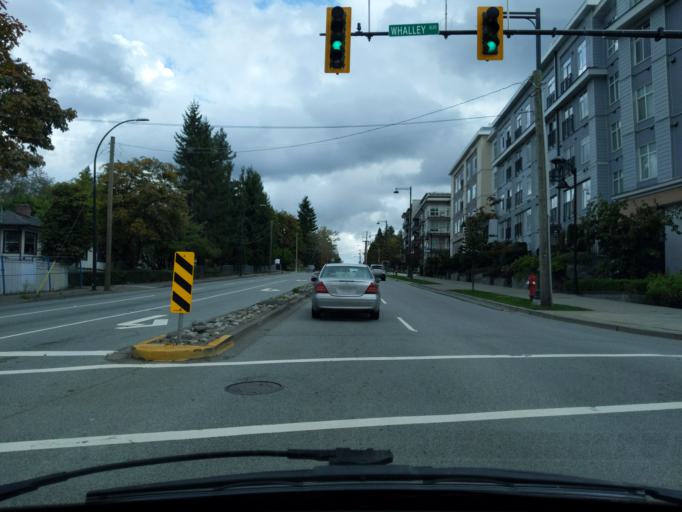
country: CA
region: British Columbia
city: New Westminster
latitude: 49.1988
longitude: -122.8425
